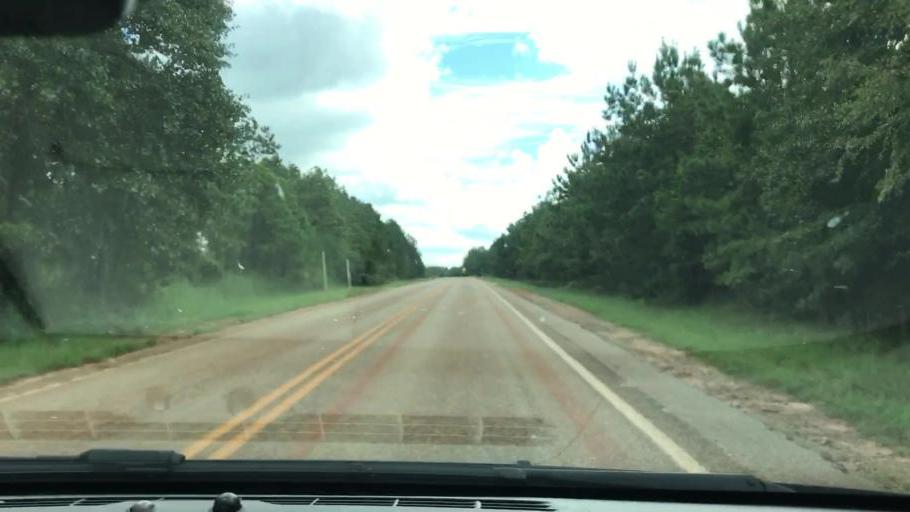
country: US
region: Georgia
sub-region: Stewart County
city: Lumpkin
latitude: 32.0723
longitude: -84.8737
